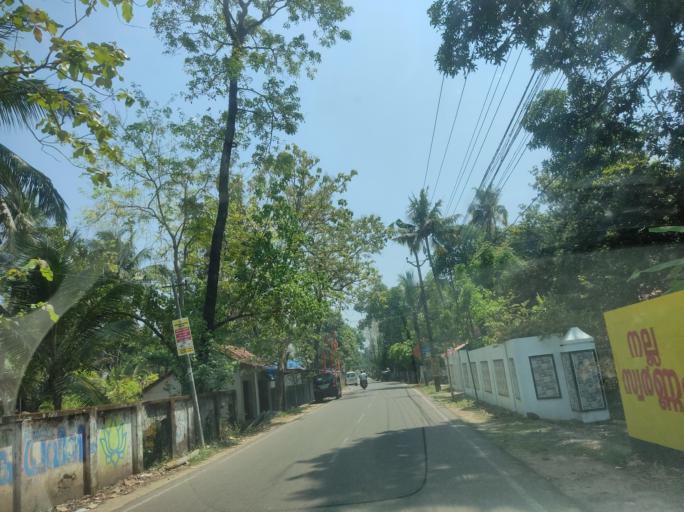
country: IN
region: Kerala
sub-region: Alappuzha
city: Kutiatodu
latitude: 9.8405
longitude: 76.2961
